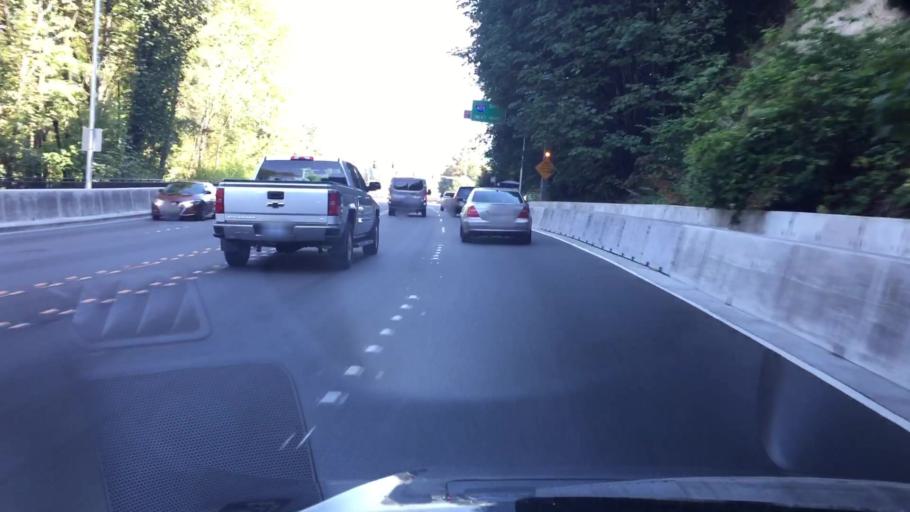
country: US
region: Washington
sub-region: King County
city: Tukwila
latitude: 47.4665
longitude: -122.2509
